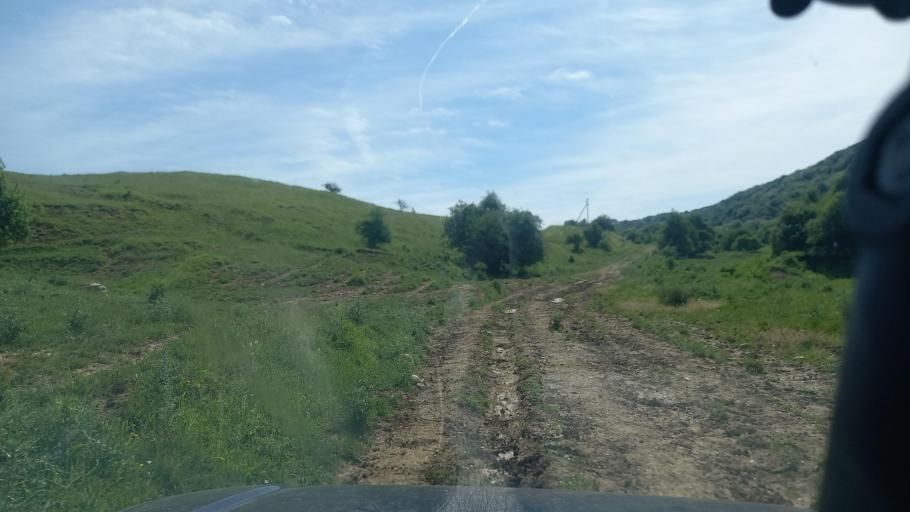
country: RU
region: Karachayevo-Cherkesiya
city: Kurdzhinovo
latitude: 44.1417
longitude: 41.0582
